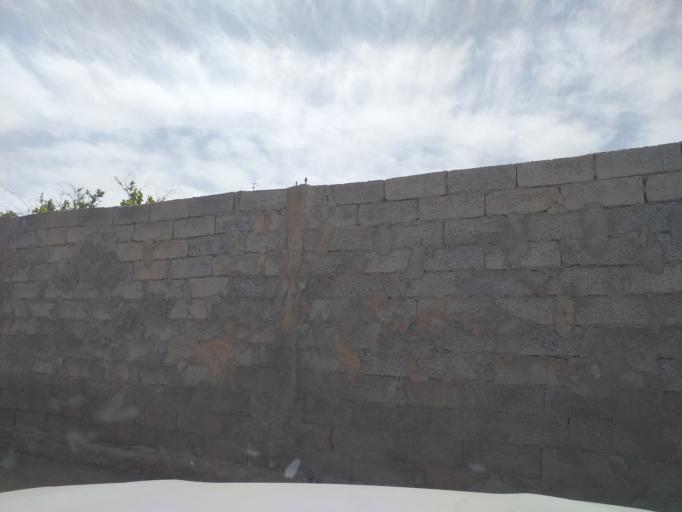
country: TN
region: Qabis
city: Gabes
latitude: 33.9490
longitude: 10.0676
